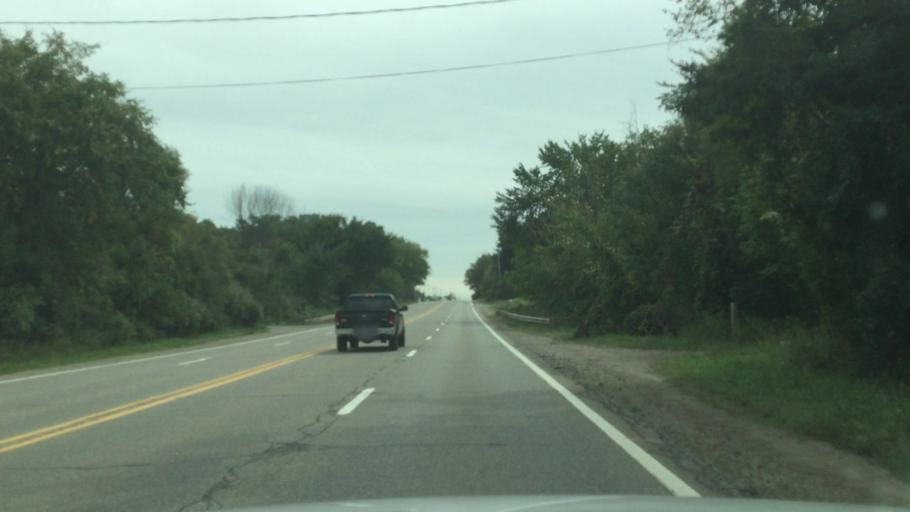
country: US
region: Michigan
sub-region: Oakland County
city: Ortonville
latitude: 42.7935
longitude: -83.5164
